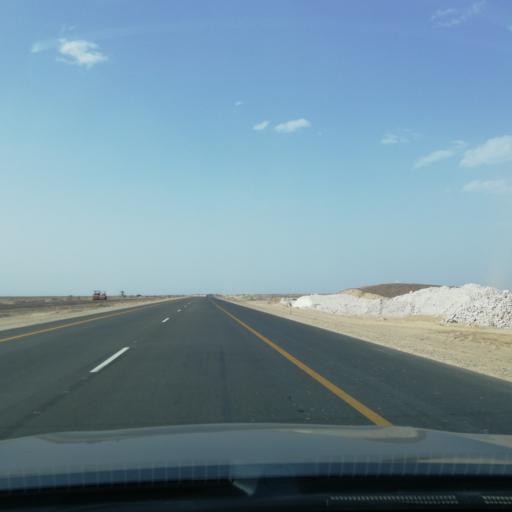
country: OM
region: Muhafazat ad Dakhiliyah
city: Adam
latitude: 22.0824
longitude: 57.5162
